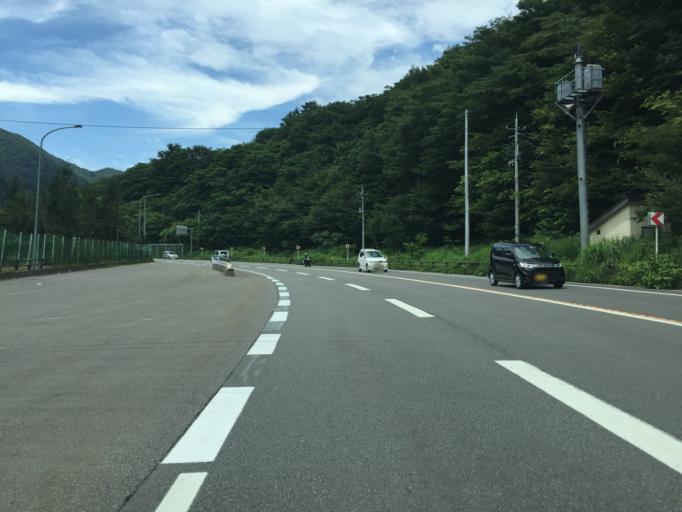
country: JP
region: Fukushima
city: Fukushima-shi
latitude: 37.8420
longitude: 140.3089
